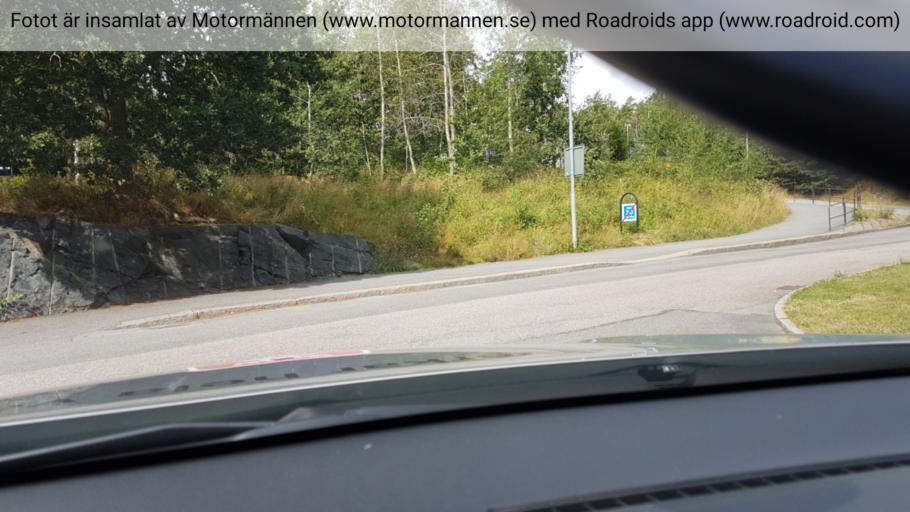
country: SE
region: Vaestra Goetaland
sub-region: Goteborg
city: Majorna
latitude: 57.7518
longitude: 11.9176
